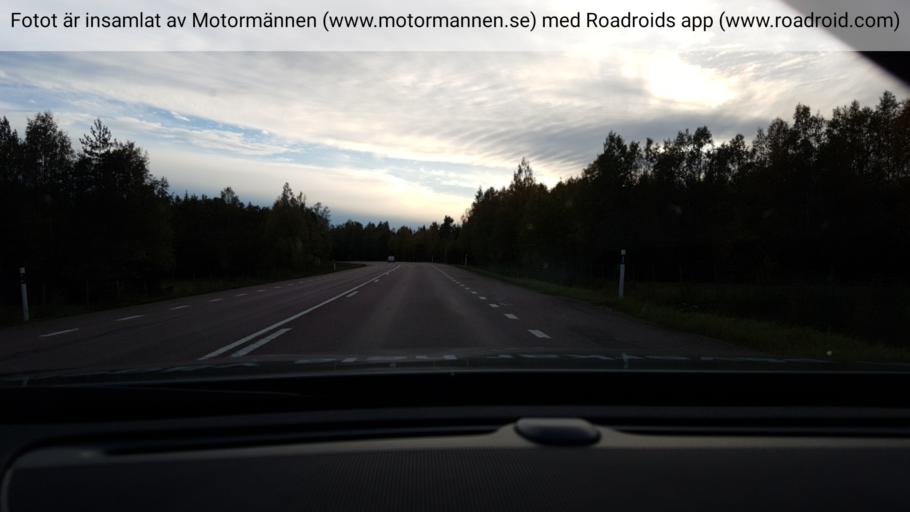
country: SE
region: Gaevleborg
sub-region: Nordanstigs Kommun
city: Bergsjoe
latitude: 61.9497
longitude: 17.2324
